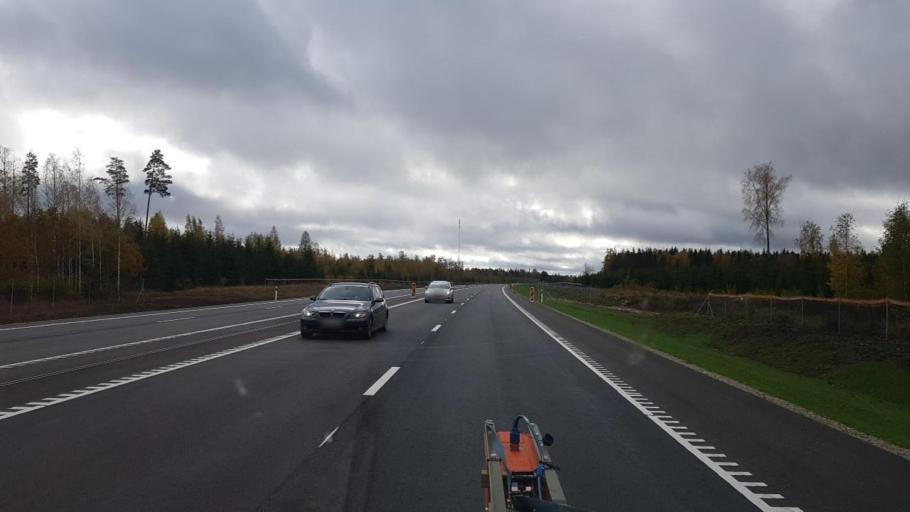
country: EE
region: Jaervamaa
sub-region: Paide linn
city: Paide
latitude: 58.9816
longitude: 25.6010
